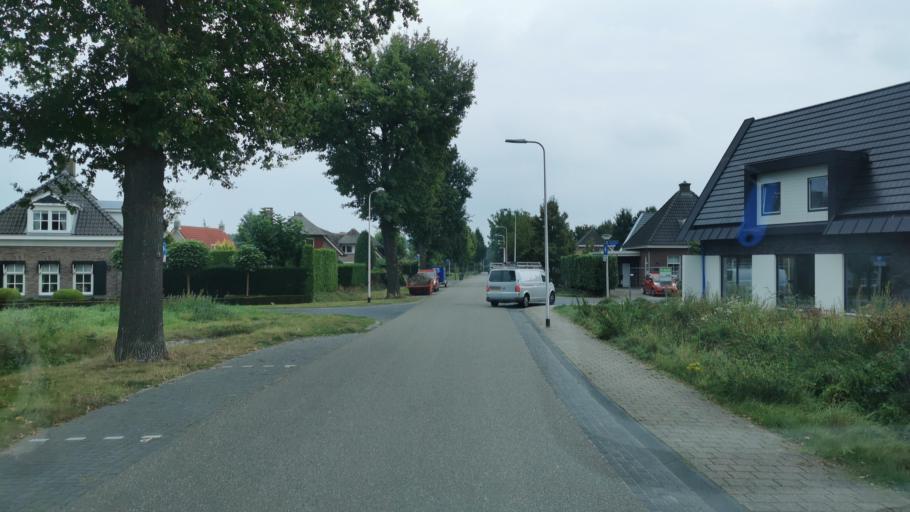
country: NL
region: Overijssel
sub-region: Gemeente Losser
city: Losser
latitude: 52.3127
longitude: 7.0026
